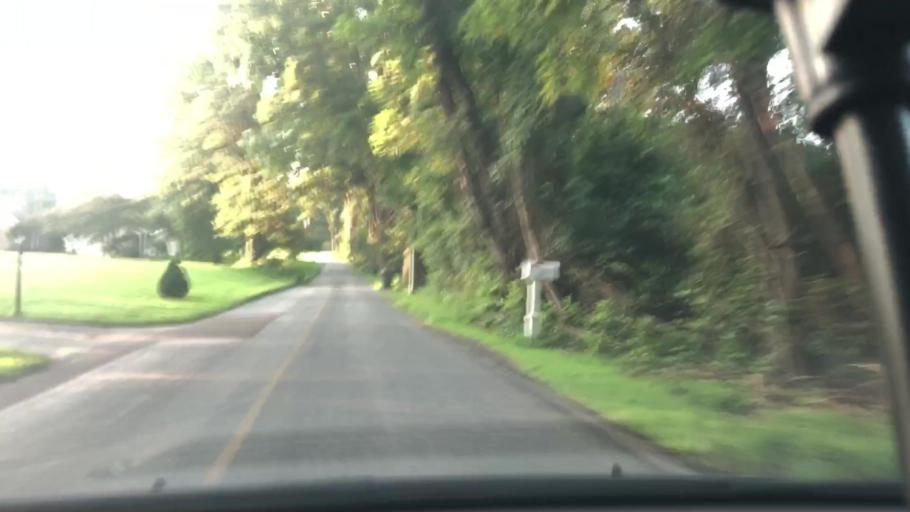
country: US
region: Pennsylvania
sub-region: Chester County
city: Kenilworth
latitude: 40.1866
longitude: -75.6439
